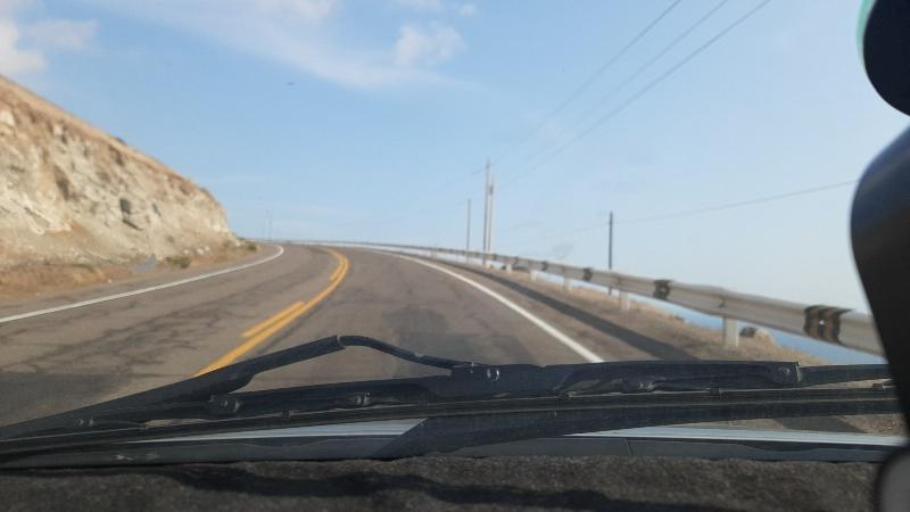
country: PE
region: Moquegua
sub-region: Provincia de Ilo
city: Ilo
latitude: -17.6829
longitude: -71.2908
